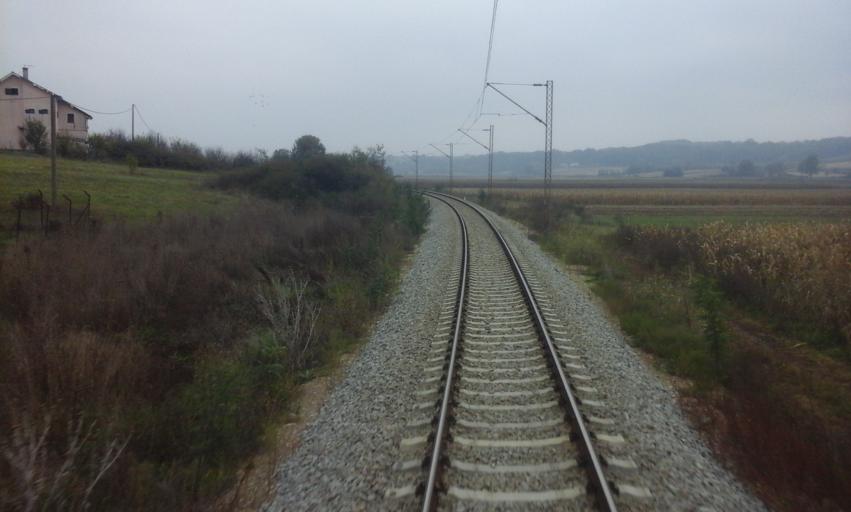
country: RS
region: Central Serbia
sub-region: Belgrade
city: Mladenovac
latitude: 44.4709
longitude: 20.6633
